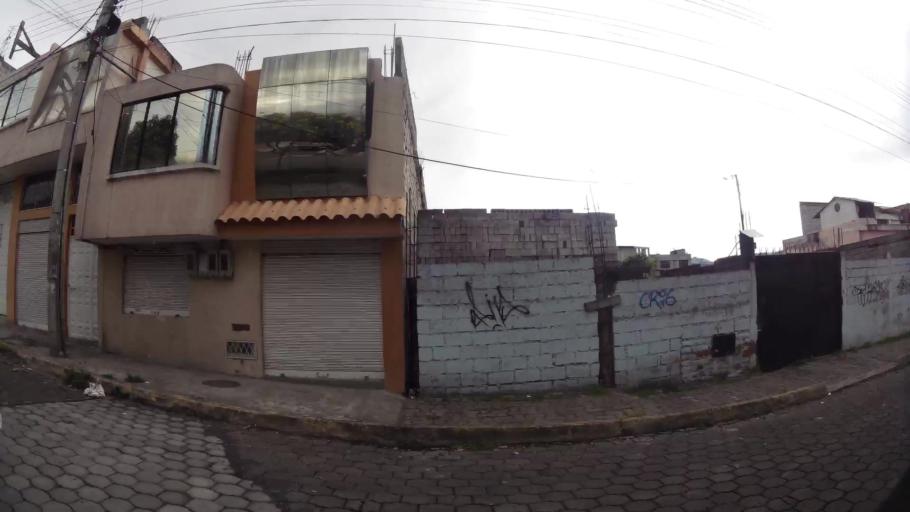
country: EC
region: Pichincha
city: Quito
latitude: -0.3086
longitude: -78.5538
